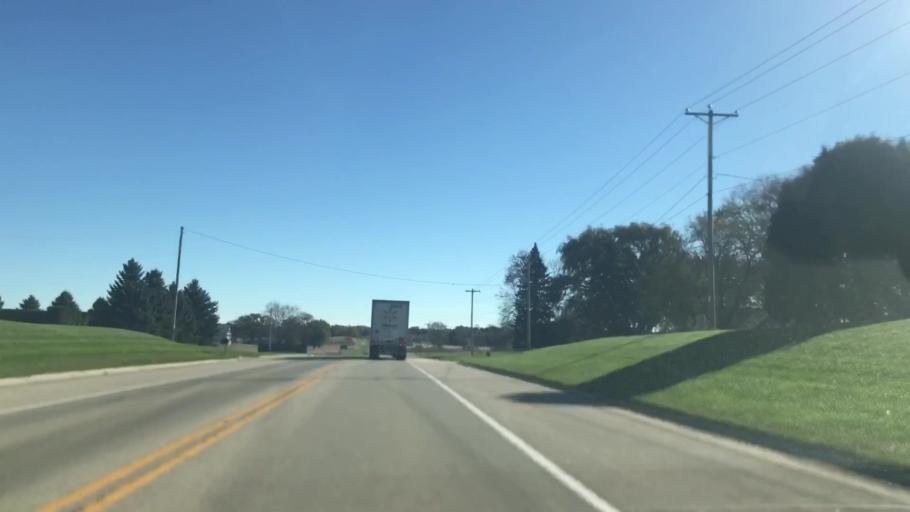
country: US
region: Wisconsin
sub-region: Dodge County
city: Juneau
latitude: 43.4446
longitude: -88.7227
